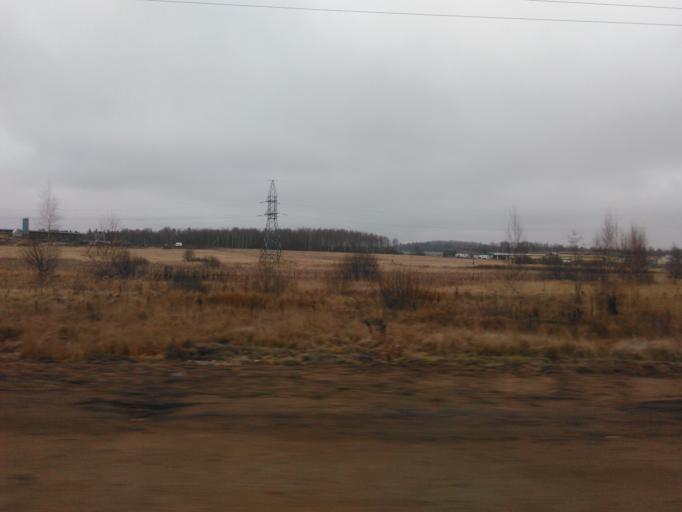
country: RU
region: Moskovskaya
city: Zelenogradskiy
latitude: 56.1120
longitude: 37.9559
